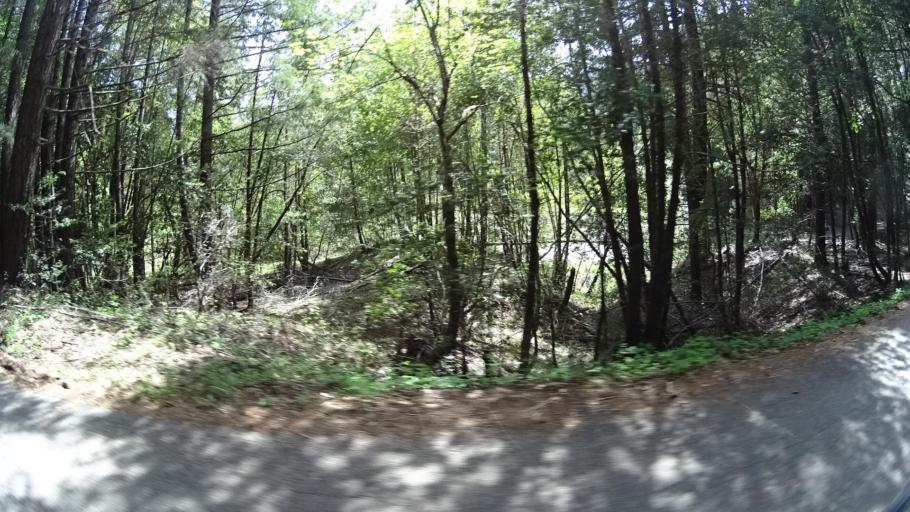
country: US
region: California
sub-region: Humboldt County
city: Redway
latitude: 40.3604
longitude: -123.7254
